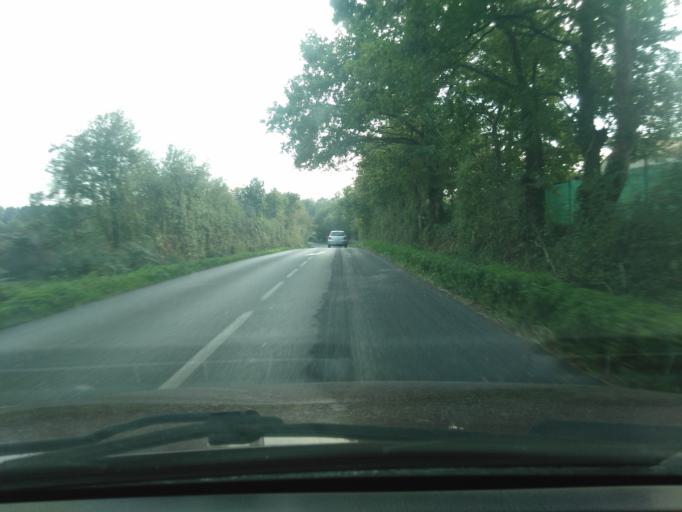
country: FR
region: Pays de la Loire
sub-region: Departement de la Vendee
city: Dompierre-sur-Yon
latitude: 46.7308
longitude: -1.3933
